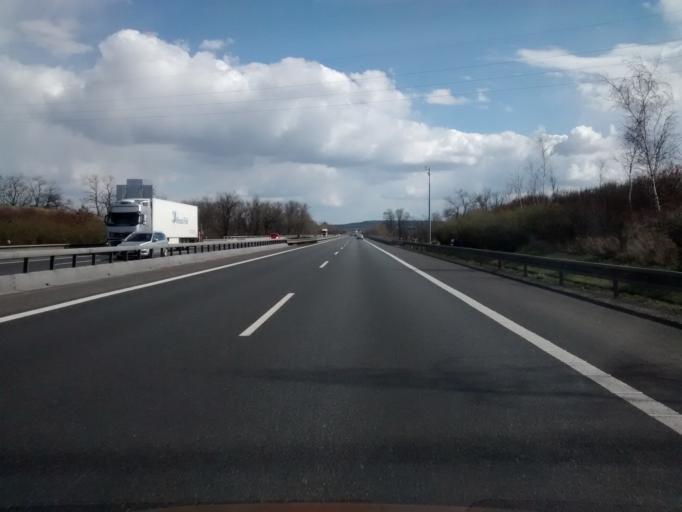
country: CZ
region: Central Bohemia
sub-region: Okres Melnik
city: Veltrusy
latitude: 50.3066
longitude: 14.3225
